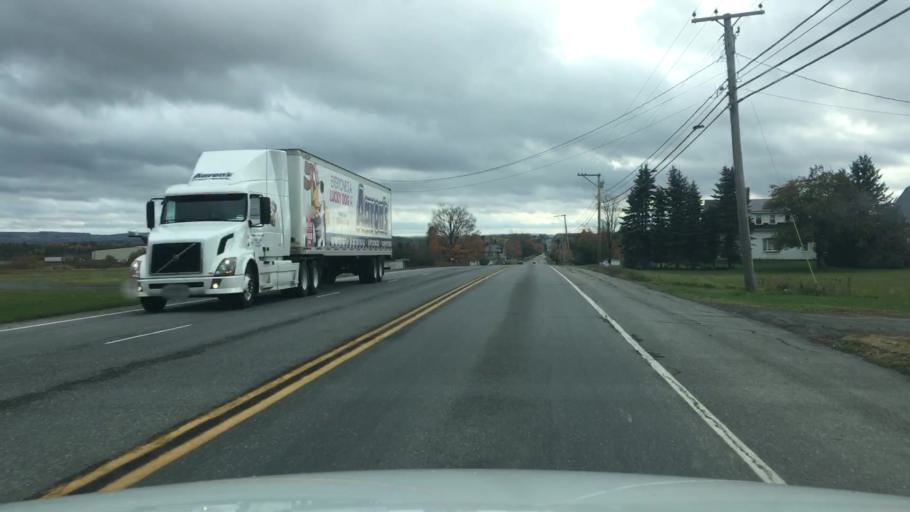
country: US
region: Maine
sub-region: Aroostook County
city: Houlton
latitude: 46.2213
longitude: -67.8411
